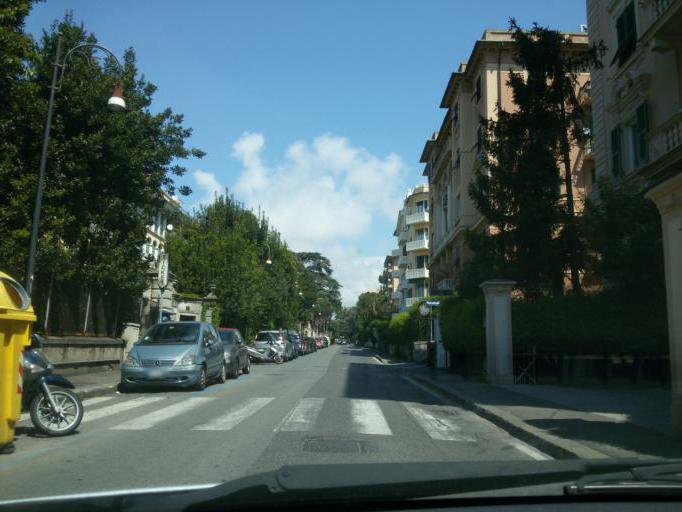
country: IT
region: Liguria
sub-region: Provincia di Genova
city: San Teodoro
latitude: 44.3955
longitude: 8.9583
